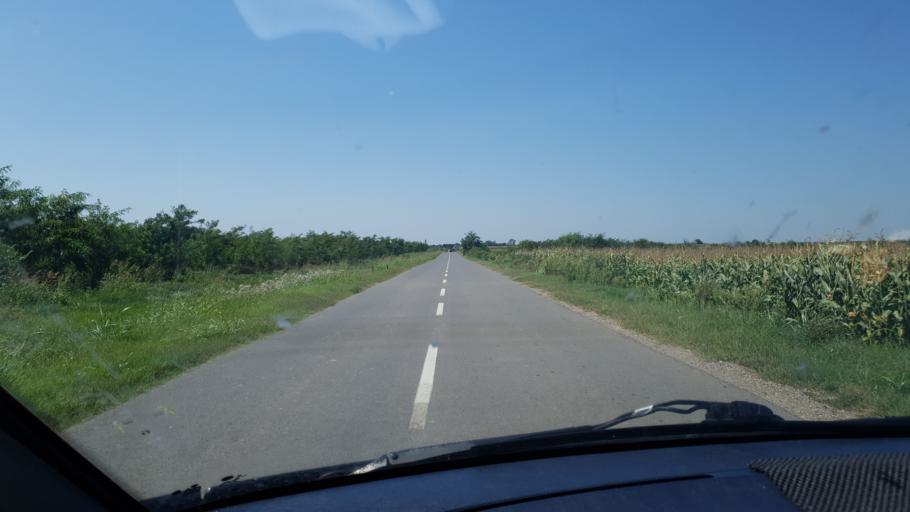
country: RS
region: Autonomna Pokrajina Vojvodina
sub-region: Juznobacki Okrug
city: Kovilj
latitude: 45.2186
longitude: 20.0561
